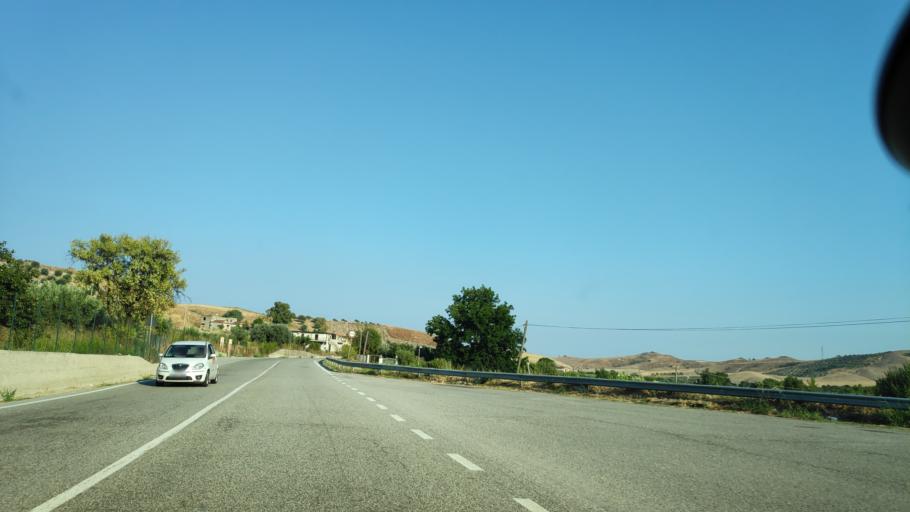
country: IT
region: Calabria
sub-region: Provincia di Reggio Calabria
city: Monasterace
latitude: 38.4860
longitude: 16.5423
